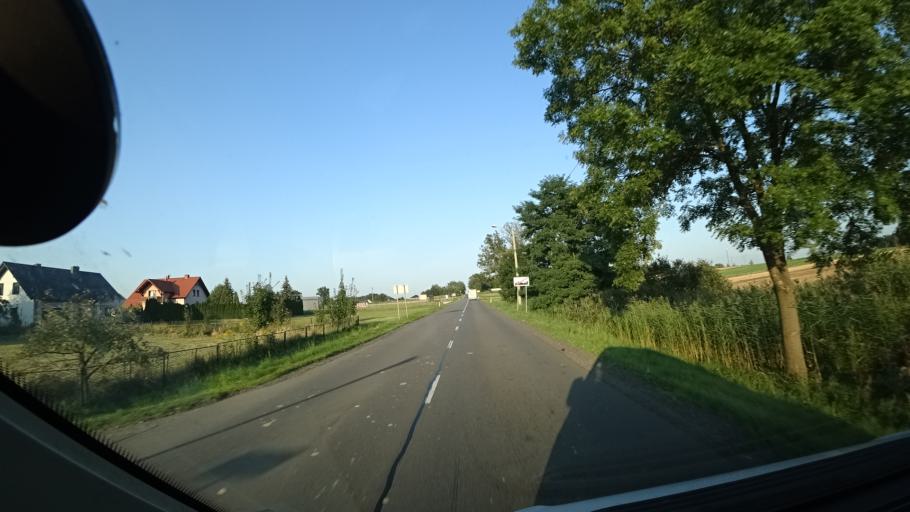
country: PL
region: Silesian Voivodeship
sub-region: Powiat gliwicki
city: Sosnicowice
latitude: 50.2744
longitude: 18.4584
